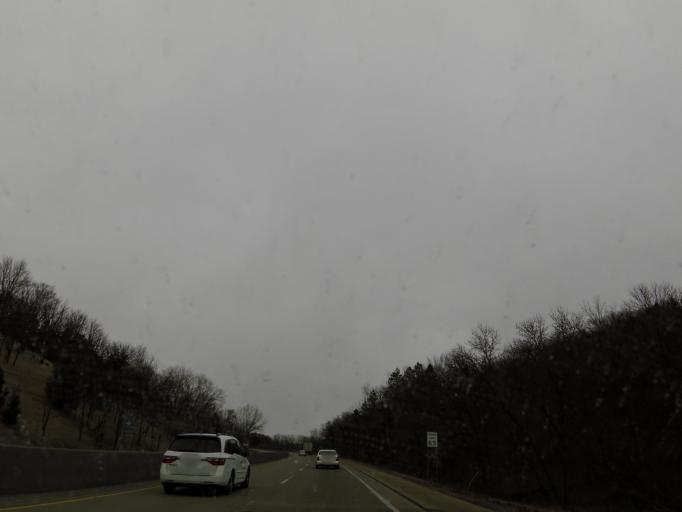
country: US
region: Minnesota
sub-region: Le Sueur County
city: Le Sueur
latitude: 44.4835
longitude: -93.8878
